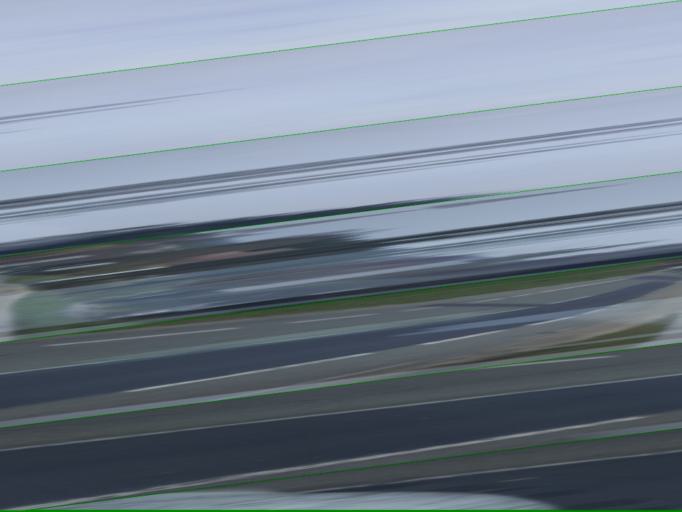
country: FR
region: Ile-de-France
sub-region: Departement des Yvelines
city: Houdan
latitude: 48.7899
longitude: 1.5901
